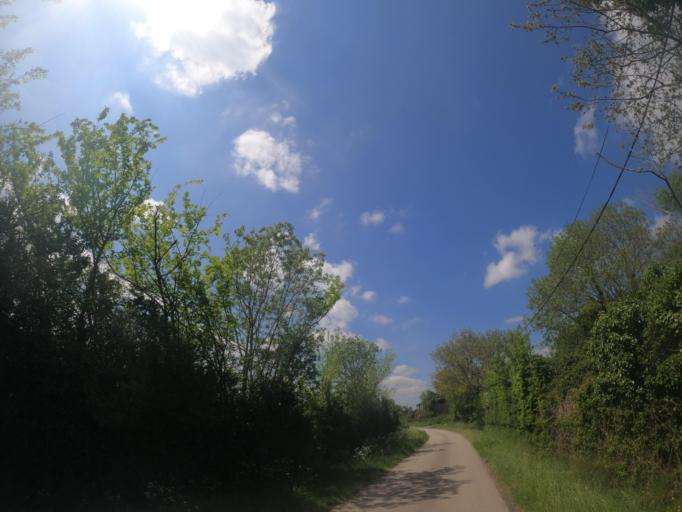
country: FR
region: Poitou-Charentes
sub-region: Departement des Deux-Sevres
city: Saint-Varent
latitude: 46.8483
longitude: -0.2774
